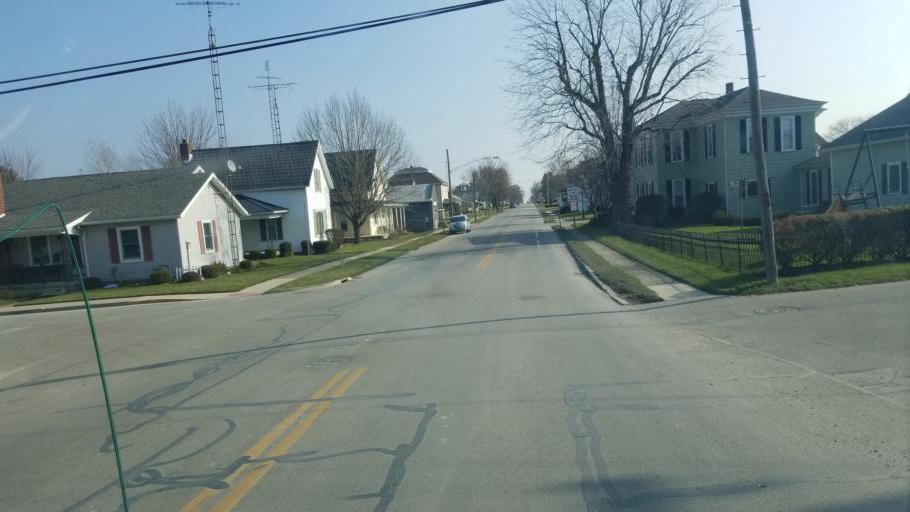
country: US
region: Ohio
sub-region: Mercer County
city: Fort Recovery
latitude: 40.4141
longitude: -84.7789
